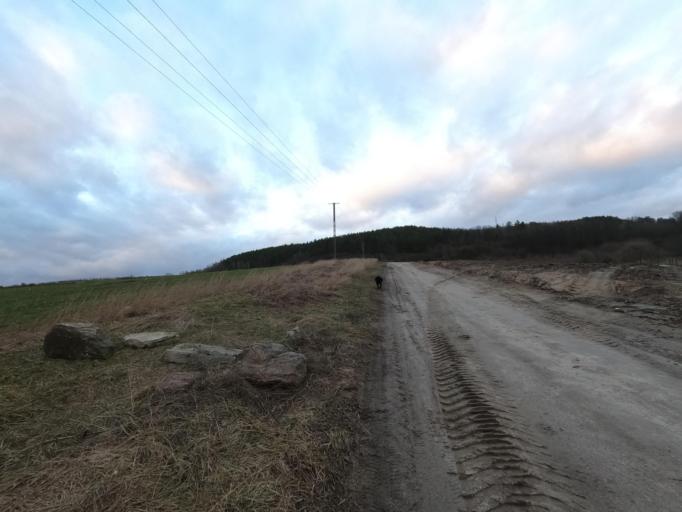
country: PL
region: Greater Poland Voivodeship
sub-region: Powiat pilski
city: Wyrzysk
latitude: 53.1146
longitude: 17.2039
